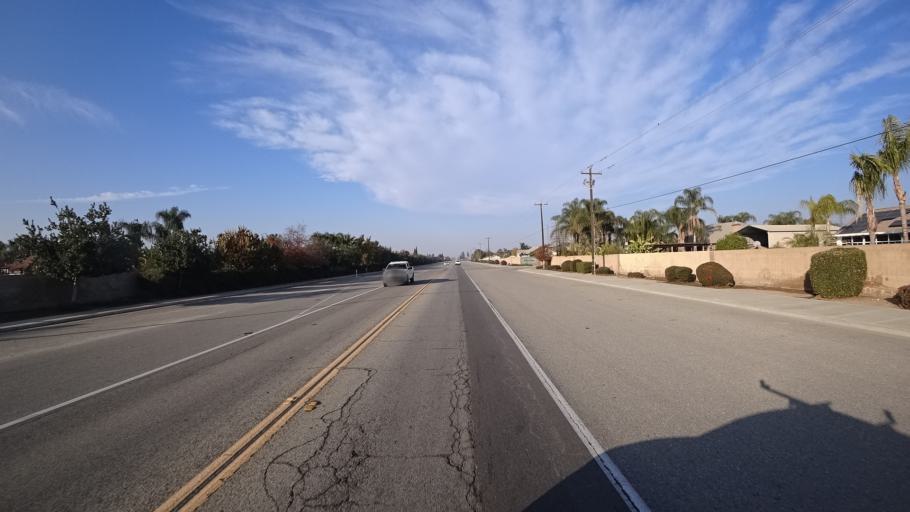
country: US
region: California
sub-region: Kern County
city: Rosedale
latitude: 35.3835
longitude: -119.1678
